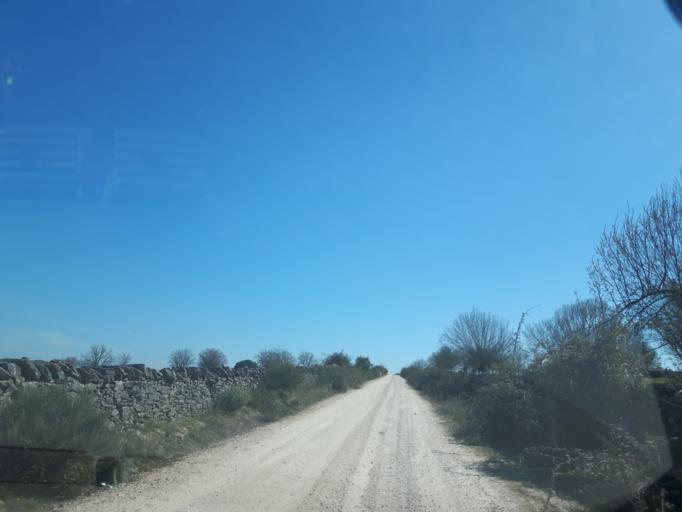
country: ES
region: Castille and Leon
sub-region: Provincia de Salamanca
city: Bermellar
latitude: 40.9624
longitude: -6.6790
